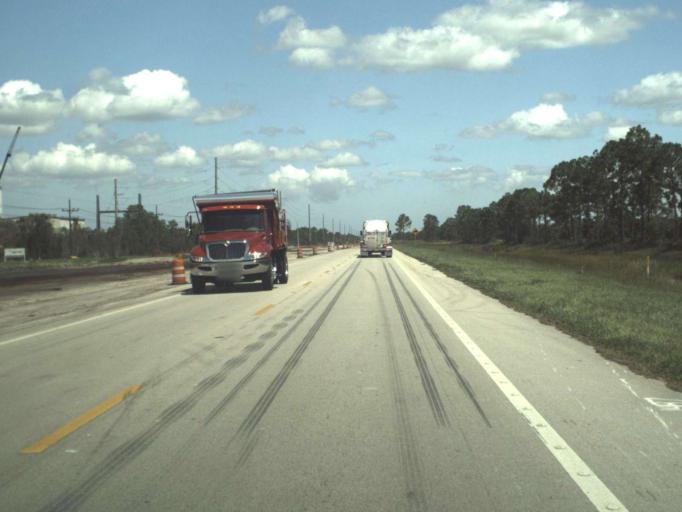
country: US
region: Florida
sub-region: Palm Beach County
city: Limestone Creek
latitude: 26.9207
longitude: -80.3185
